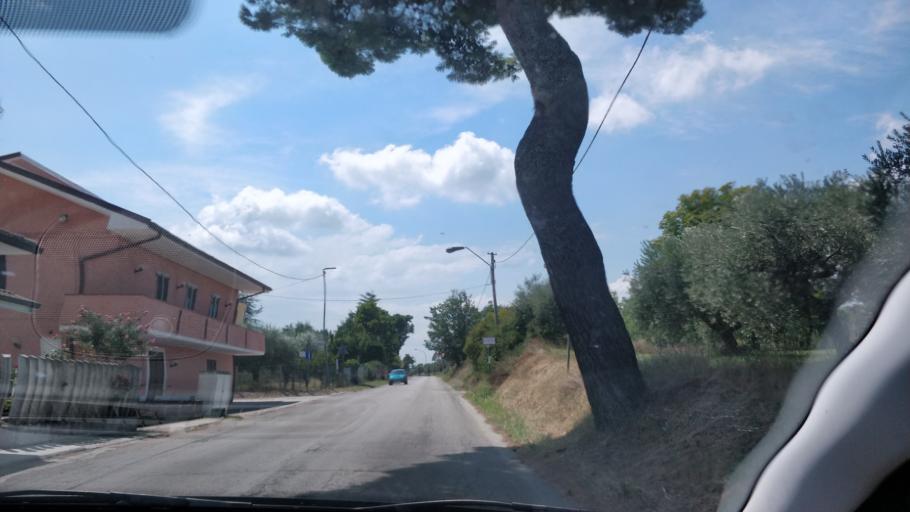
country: IT
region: Abruzzo
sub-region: Provincia di Chieti
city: Torrevecchia
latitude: 42.4021
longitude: 14.2152
